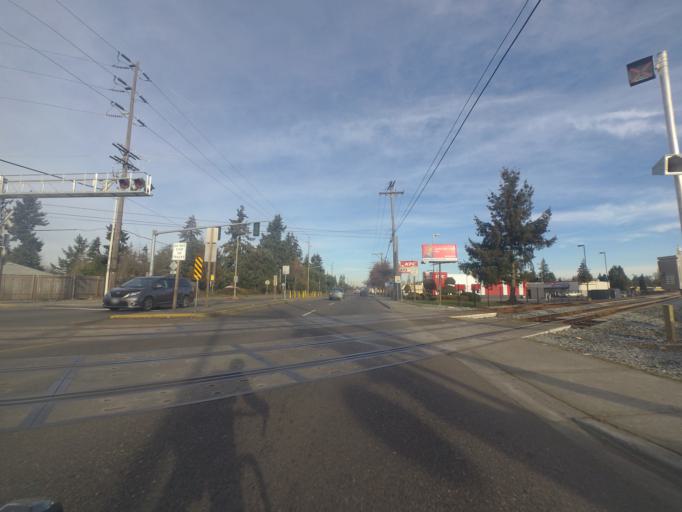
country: US
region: Washington
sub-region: Pierce County
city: McChord Air Force Base
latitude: 47.1500
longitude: -122.5043
